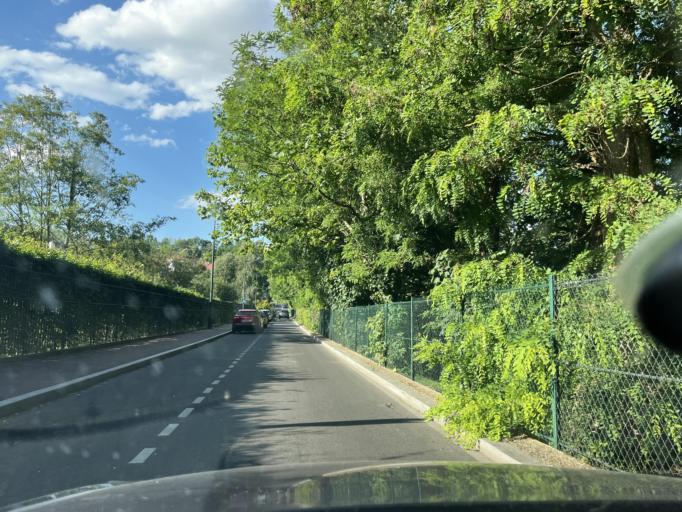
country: FR
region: Ile-de-France
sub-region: Departement des Hauts-de-Seine
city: Le Plessis-Robinson
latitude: 48.7842
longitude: 2.2718
